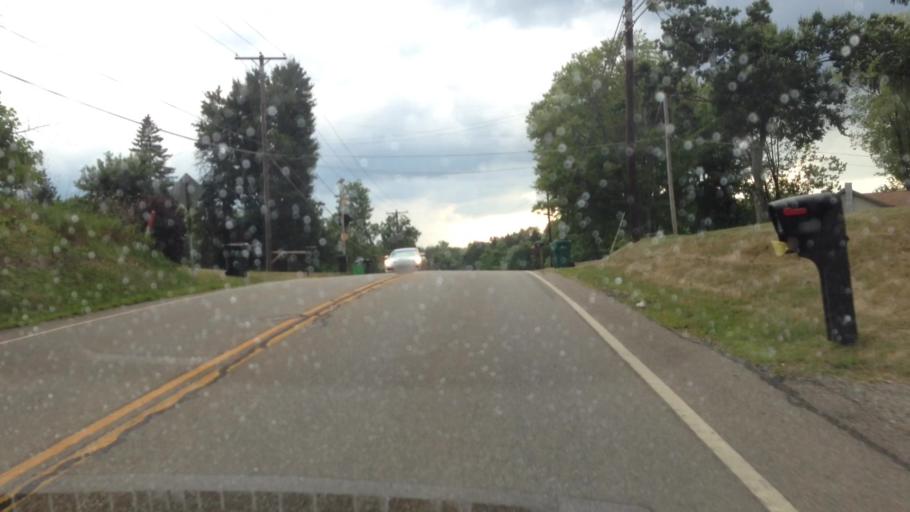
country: US
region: Ohio
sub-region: Stark County
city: Uniontown
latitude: 40.9763
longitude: -81.4276
